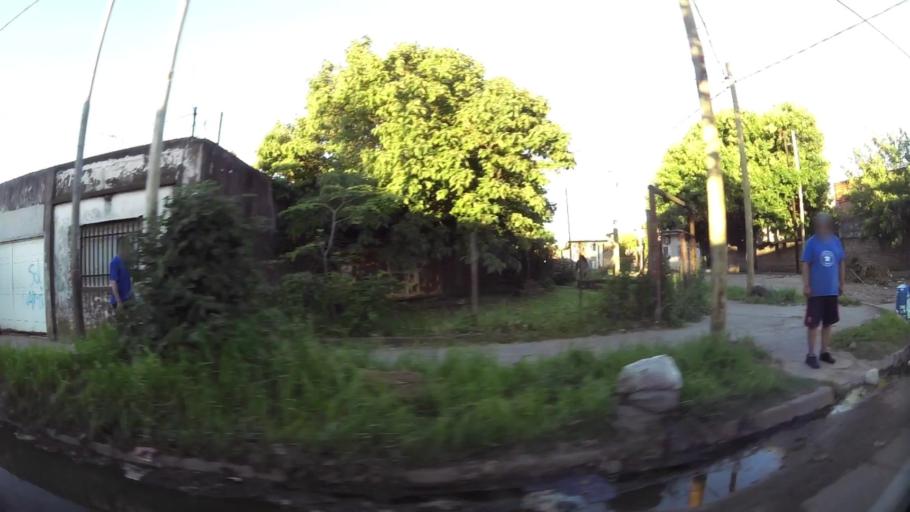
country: AR
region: Buenos Aires
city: San Justo
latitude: -34.7334
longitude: -58.6067
